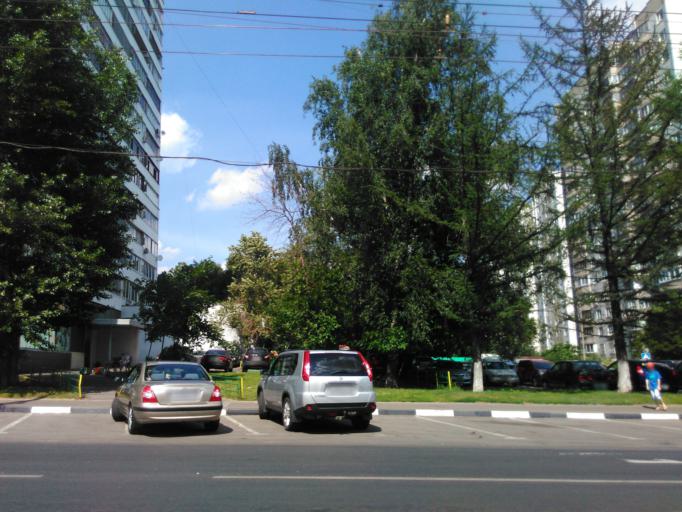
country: RU
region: Moskovskaya
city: Cheremushki
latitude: 55.6642
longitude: 37.5497
